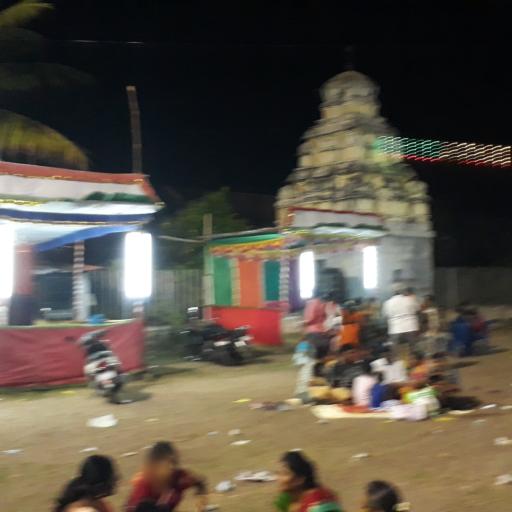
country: IN
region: Tamil Nadu
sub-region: Kancheepuram
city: Kanchipuram
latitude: 12.8467
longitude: 79.7003
